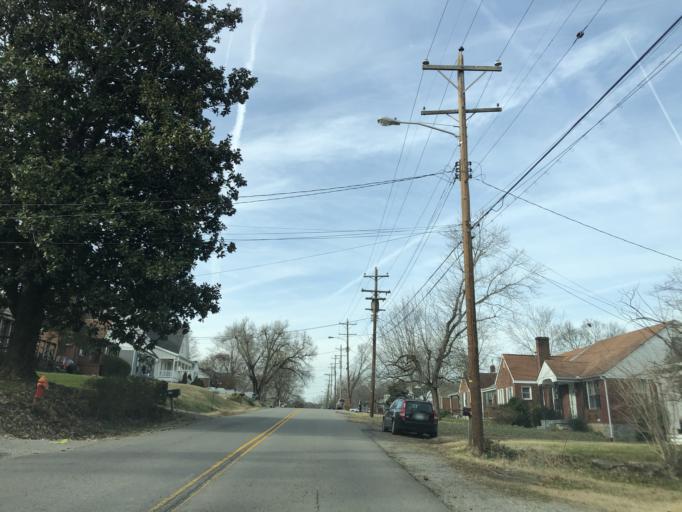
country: US
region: Tennessee
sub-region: Davidson County
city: Nashville
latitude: 36.2167
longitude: -86.7219
